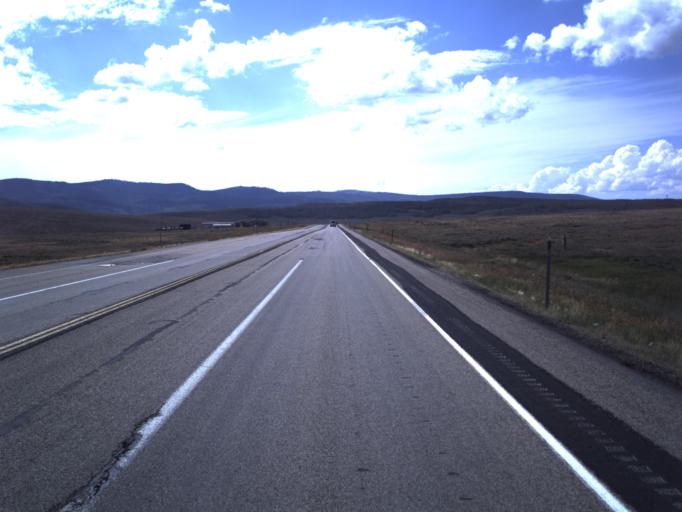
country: US
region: Utah
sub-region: Wasatch County
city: Heber
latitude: 40.2389
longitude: -111.1428
